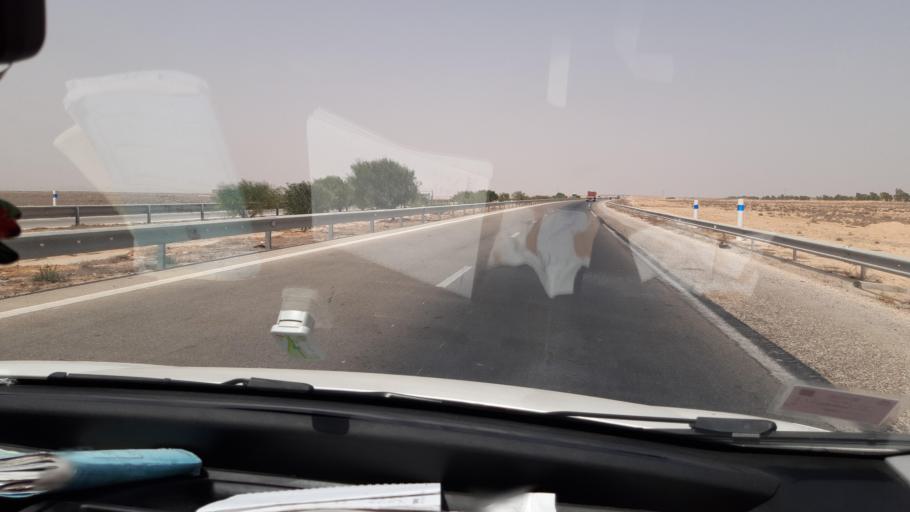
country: TN
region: Qabis
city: Gabes
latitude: 33.9195
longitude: 9.9670
